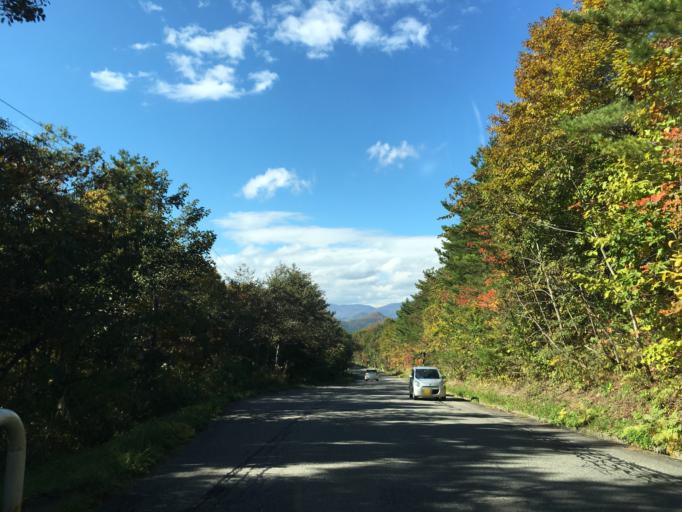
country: JP
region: Fukushima
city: Inawashiro
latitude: 37.6071
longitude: 140.2321
